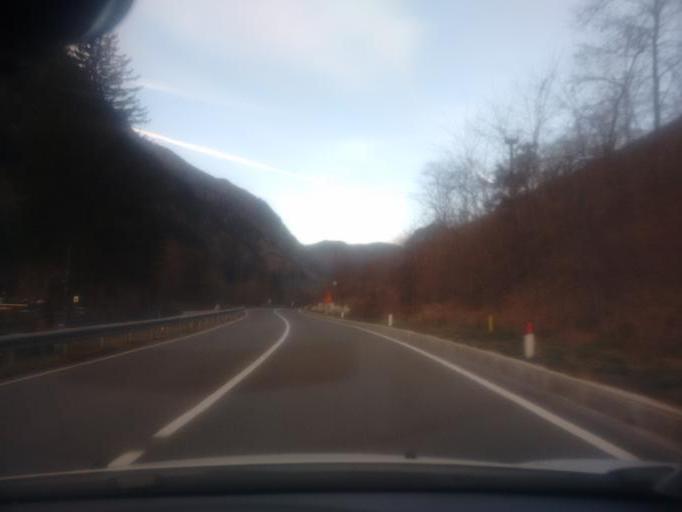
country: IT
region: Trentino-Alto Adige
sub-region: Bolzano
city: Fortezza
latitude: 46.7981
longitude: 11.5999
